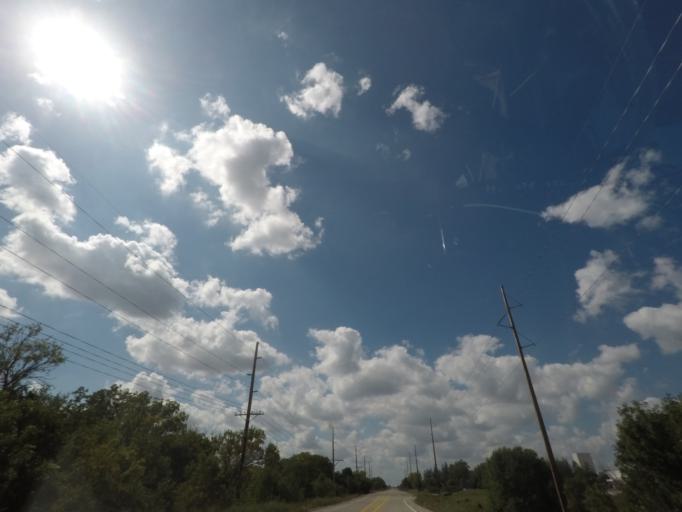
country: US
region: Iowa
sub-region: Story County
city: Ames
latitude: 42.0230
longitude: -93.5634
